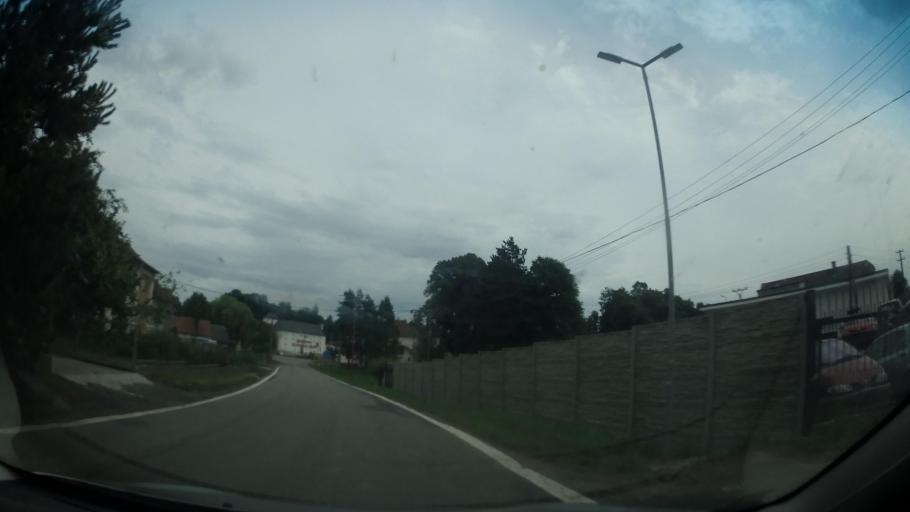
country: CZ
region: Vysocina
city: Bystrice nad Pernstejnem
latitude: 49.4754
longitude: 16.2047
